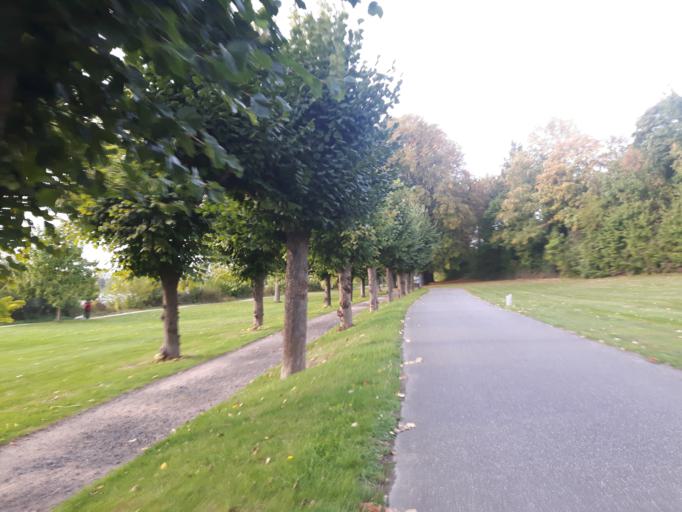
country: DE
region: Rheinland-Pfalz
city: Bad Honningen
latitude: 50.5215
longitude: 7.3000
